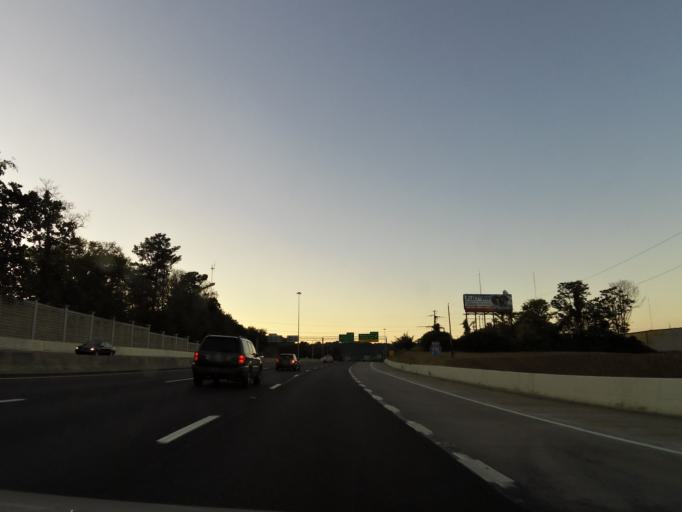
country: US
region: Tennessee
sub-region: Knox County
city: Knoxville
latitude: 35.9784
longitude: -83.9363
